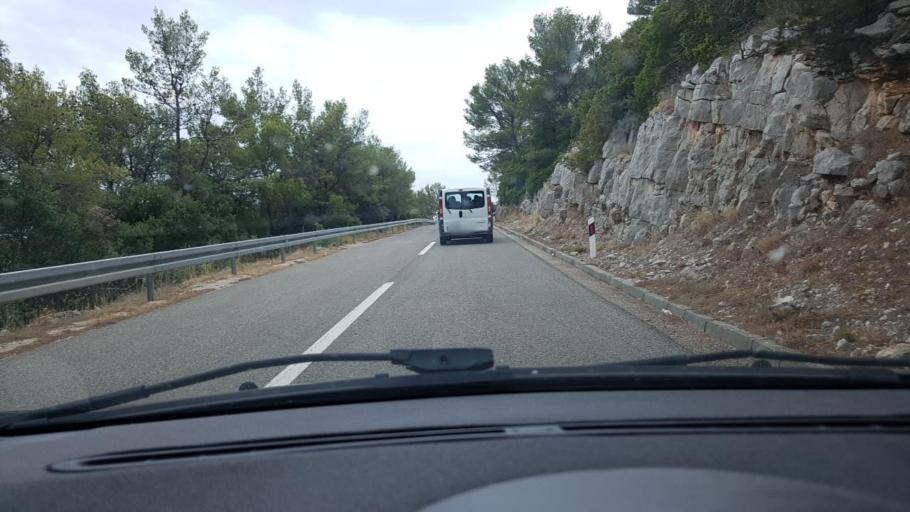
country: HR
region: Dubrovacko-Neretvanska
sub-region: Grad Korcula
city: Zrnovo
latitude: 42.9390
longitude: 17.0234
